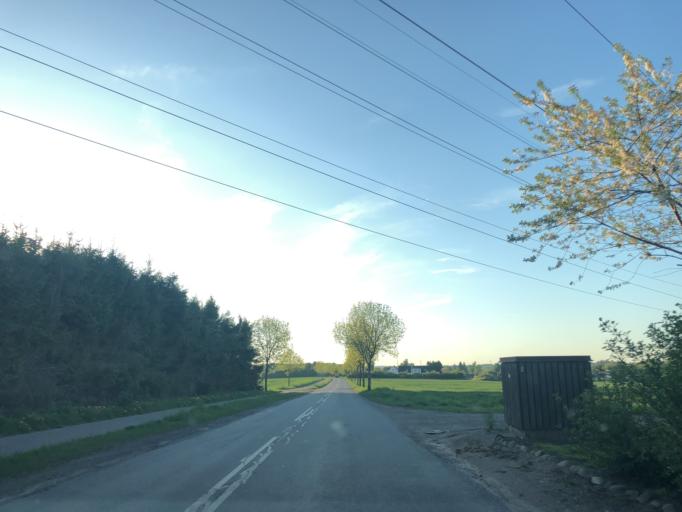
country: DK
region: Zealand
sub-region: Koge Kommune
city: Bjaeverskov
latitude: 55.4461
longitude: 12.0427
